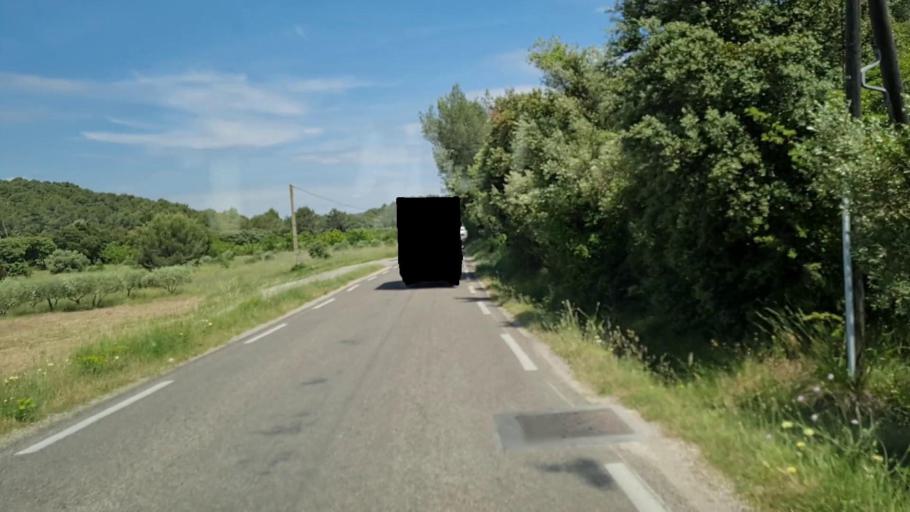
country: FR
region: Languedoc-Roussillon
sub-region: Departement du Gard
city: Saint-Gervasy
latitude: 43.8817
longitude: 4.4682
